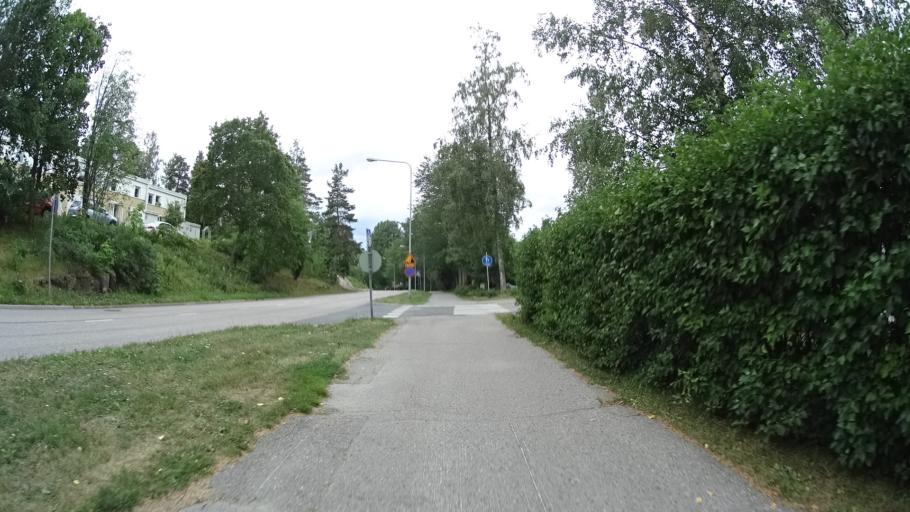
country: FI
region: Uusimaa
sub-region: Helsinki
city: Espoo
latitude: 60.1344
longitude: 24.6677
